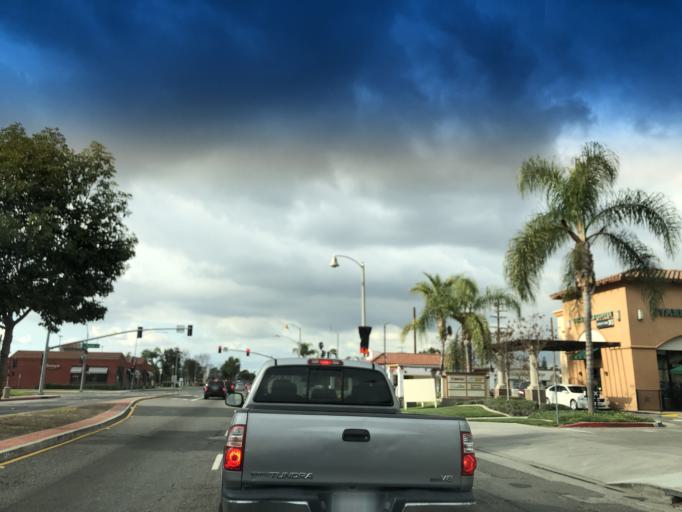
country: US
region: California
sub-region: Los Angeles County
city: Pico Rivera
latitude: 33.9990
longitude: -118.0784
